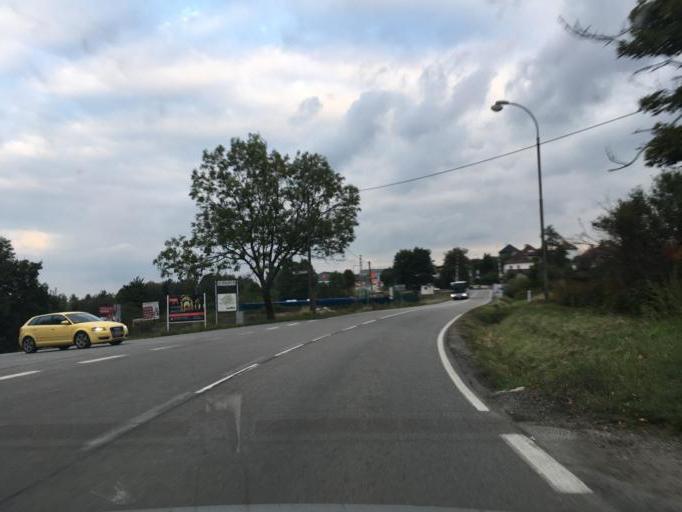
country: CZ
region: Vysocina
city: Starec
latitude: 49.2098
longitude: 15.8526
